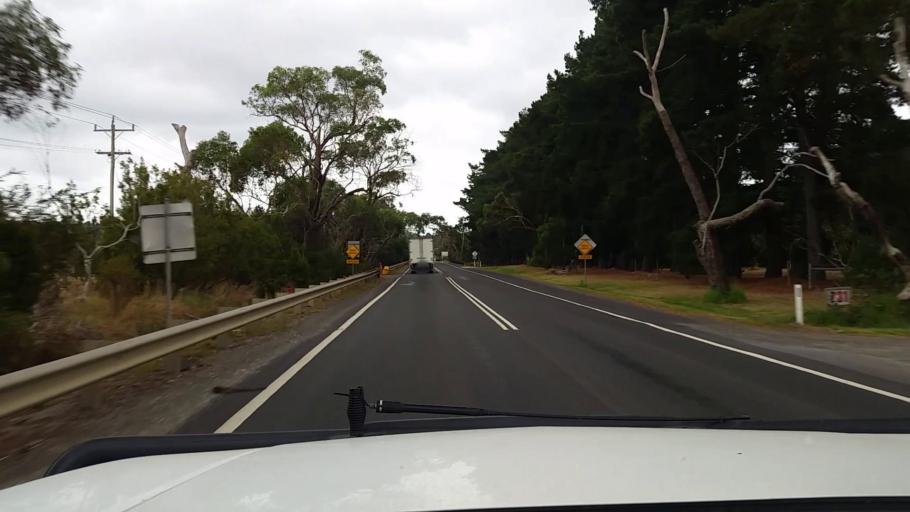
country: AU
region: Victoria
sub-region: Mornington Peninsula
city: Baxter
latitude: -38.2023
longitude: 145.1532
